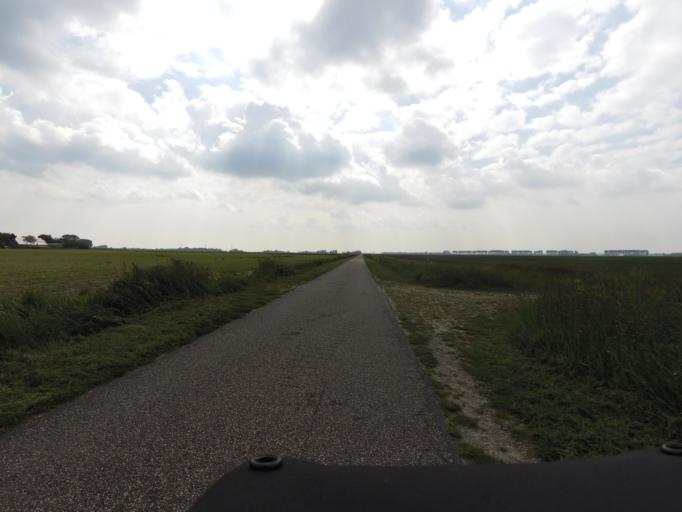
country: NL
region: Zeeland
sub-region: Gemeente Noord-Beveland
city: Kamperland
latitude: 51.6006
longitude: 3.8048
